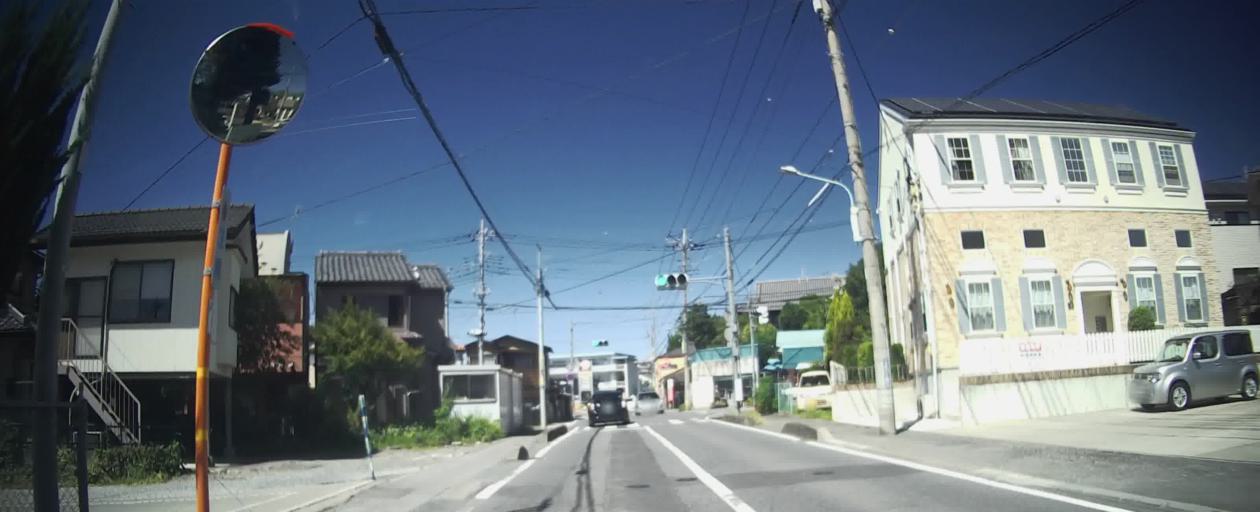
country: JP
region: Gunma
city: Maebashi-shi
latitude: 36.4002
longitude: 139.0565
